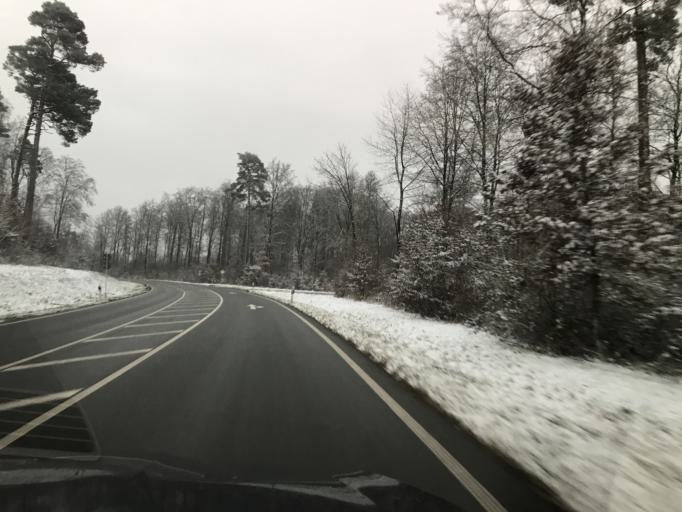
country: DE
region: Baden-Wuerttemberg
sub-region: Regierungsbezirk Stuttgart
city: Altbach
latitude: 48.7448
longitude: 9.3589
